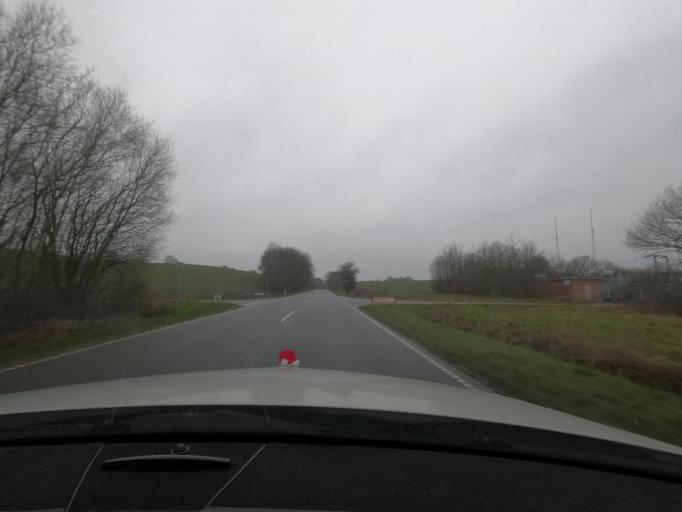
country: DK
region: South Denmark
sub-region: Haderslev Kommune
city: Haderslev
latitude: 55.1821
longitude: 9.4018
